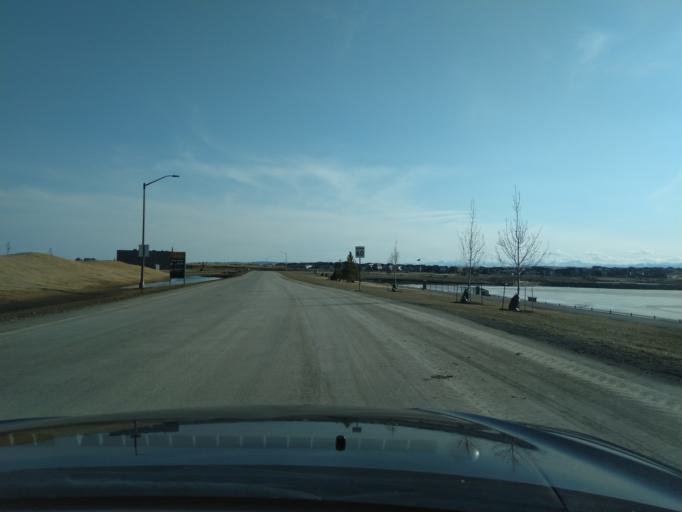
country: CA
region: Alberta
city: Cochrane
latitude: 51.1188
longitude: -114.3886
